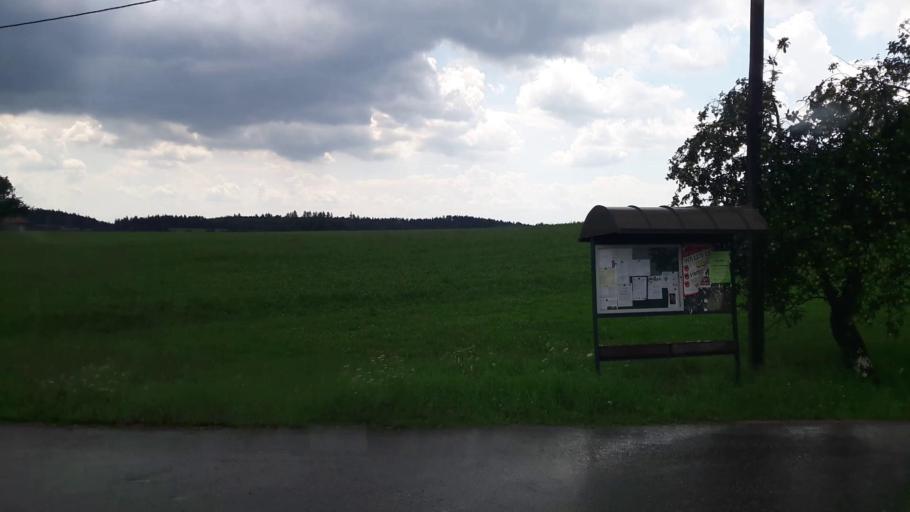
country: AT
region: Lower Austria
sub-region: Politischer Bezirk Krems
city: Aggsbach
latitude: 48.2956
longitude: 15.3704
